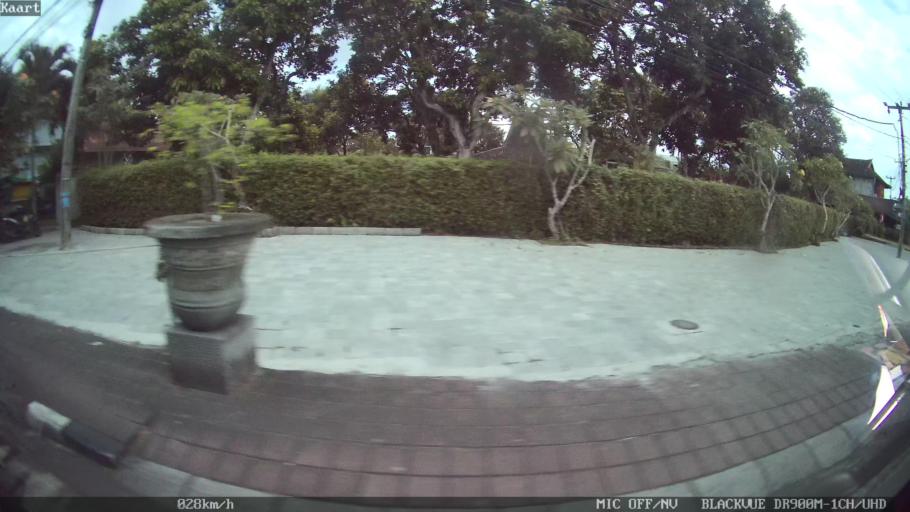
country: ID
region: Bali
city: Banjar Karangsuling
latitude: -8.6077
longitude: 115.1724
